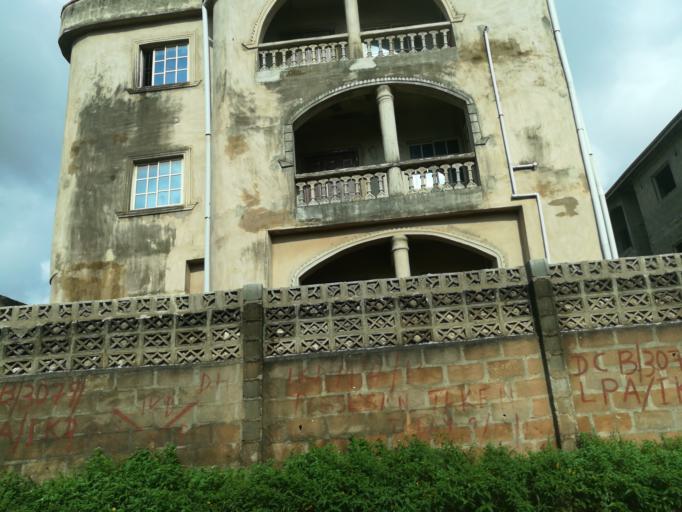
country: NG
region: Lagos
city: Ikorodu
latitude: 6.5994
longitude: 3.5056
